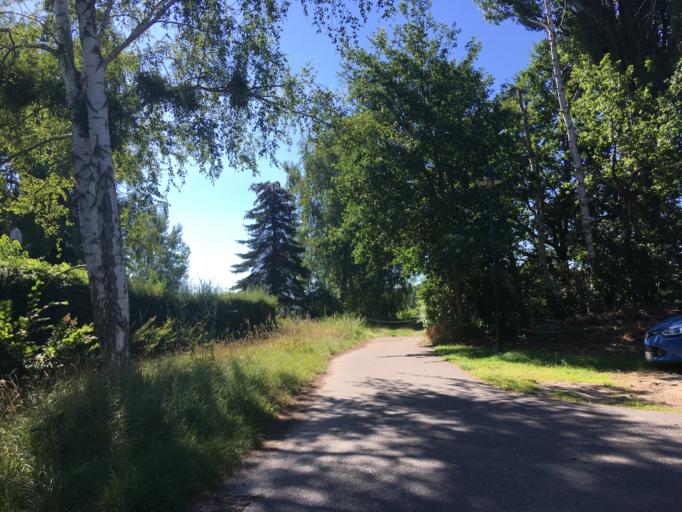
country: DE
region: Brandenburg
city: Altlandsberg
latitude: 52.5465
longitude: 13.7170
